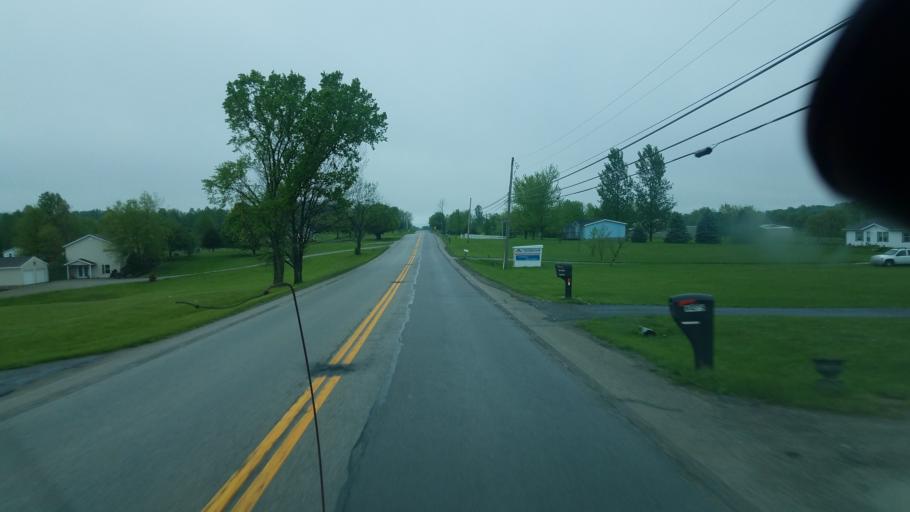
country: US
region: Ohio
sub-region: Highland County
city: Hillsboro
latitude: 39.2709
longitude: -83.5965
